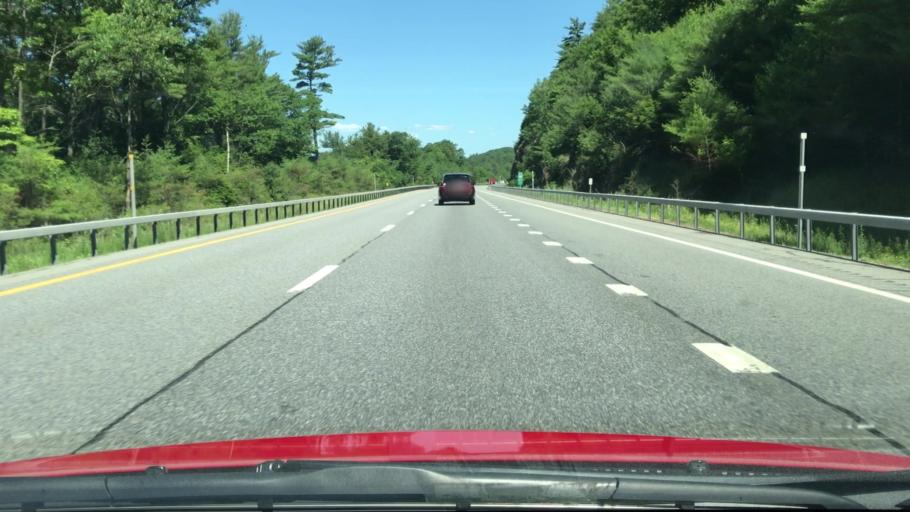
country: US
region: New York
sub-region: Warren County
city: Warrensburg
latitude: 43.4645
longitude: -73.7438
